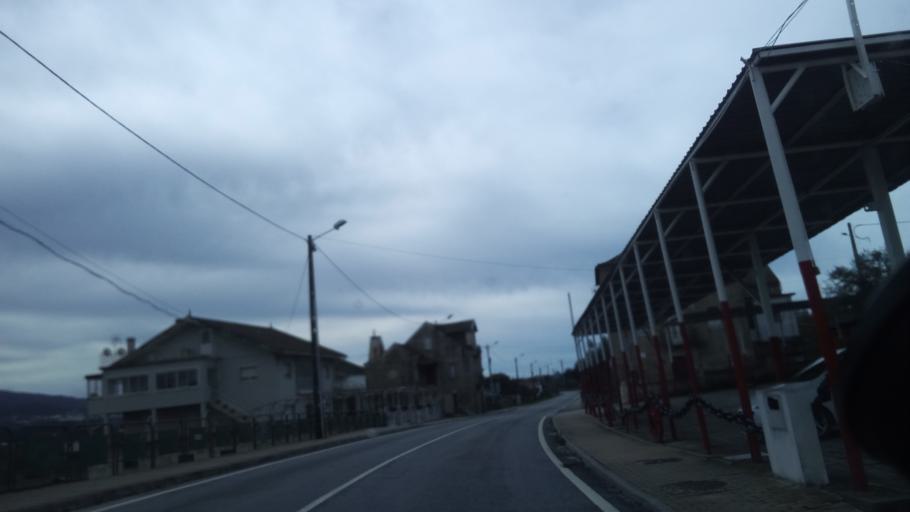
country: PT
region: Guarda
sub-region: Seia
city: Seia
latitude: 40.4658
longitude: -7.6840
